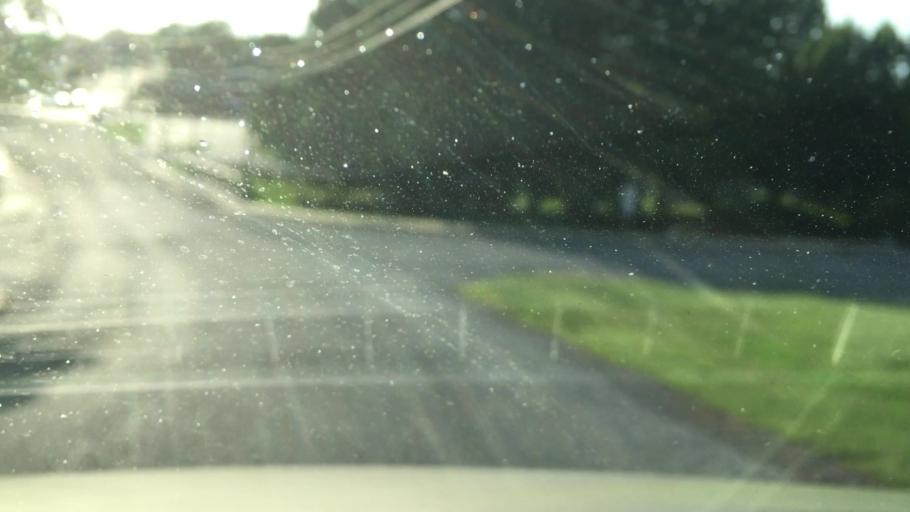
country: US
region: Oklahoma
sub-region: Cherokee County
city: Tahlequah
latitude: 35.9137
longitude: -94.9677
